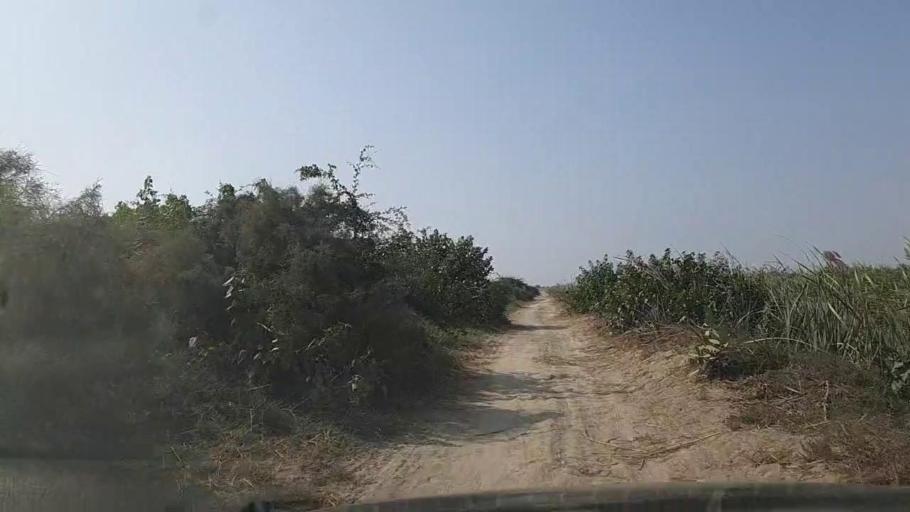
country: PK
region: Sindh
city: Gharo
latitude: 24.7179
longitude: 67.6617
